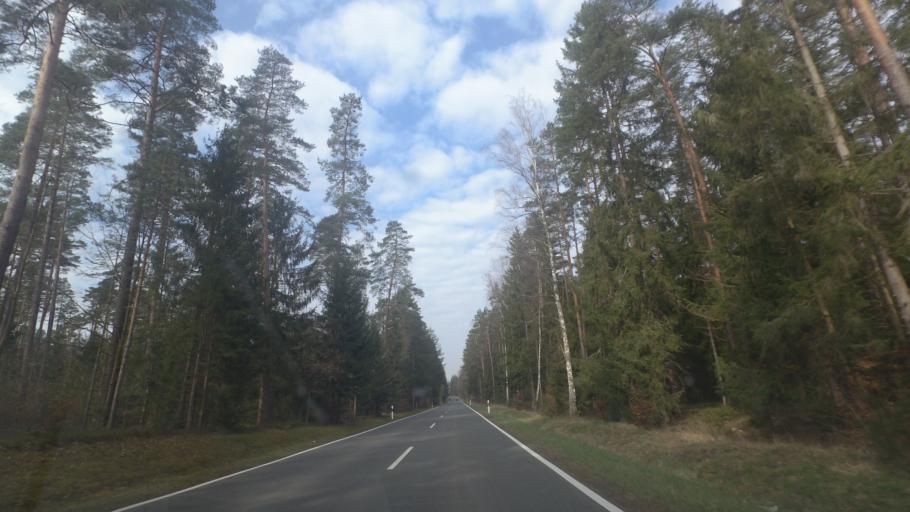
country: DE
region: Bavaria
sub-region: Regierungsbezirk Mittelfranken
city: Feucht
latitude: 49.4185
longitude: 11.2325
